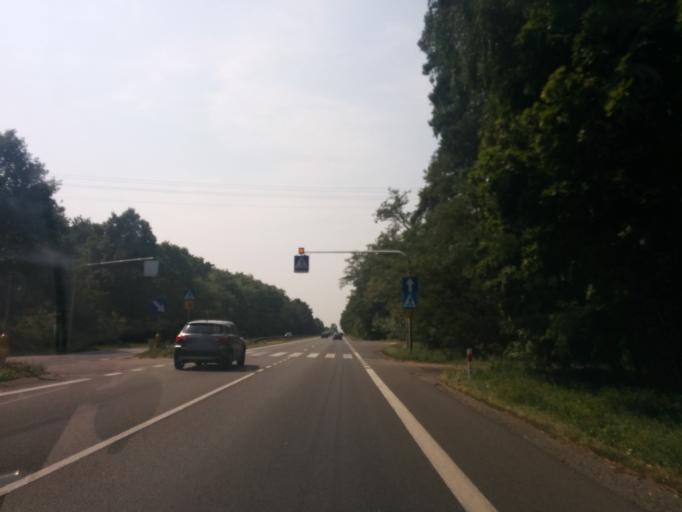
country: PL
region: Lodz Voivodeship
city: Zabia Wola
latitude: 52.0604
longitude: 20.7366
